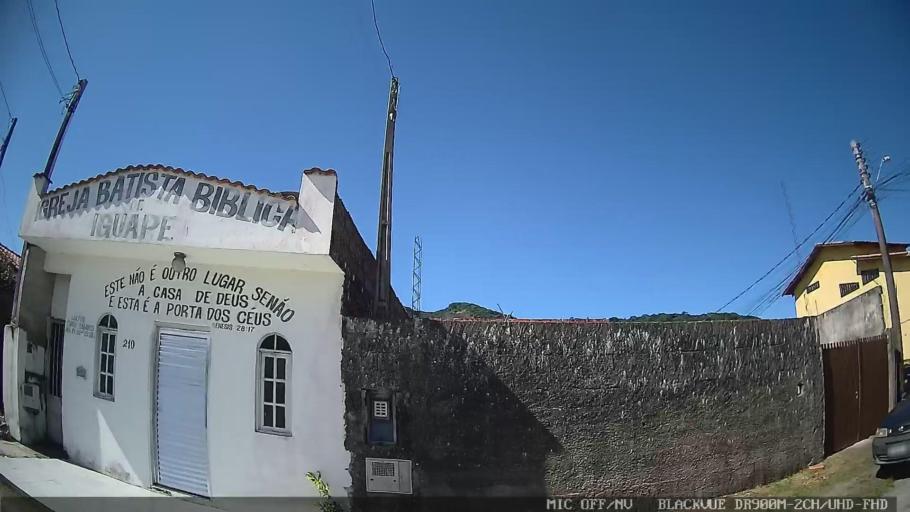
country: BR
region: Sao Paulo
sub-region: Iguape
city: Iguape
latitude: -24.7026
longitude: -47.5568
